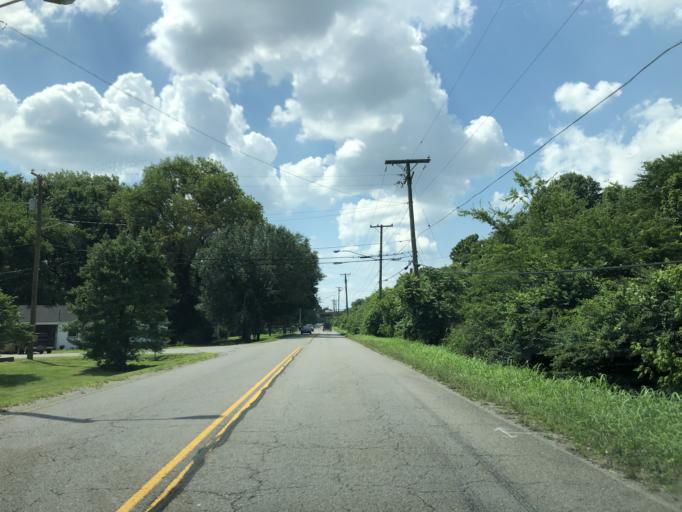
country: US
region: Tennessee
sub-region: Davidson County
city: Oak Hill
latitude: 36.1217
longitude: -86.7337
